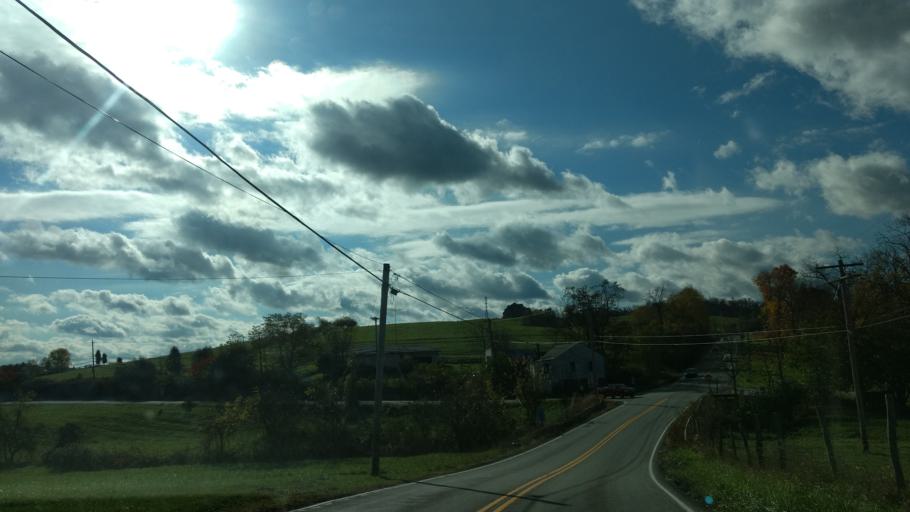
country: US
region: Pennsylvania
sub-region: Westmoreland County
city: Fellsburg
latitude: 40.1692
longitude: -79.8181
